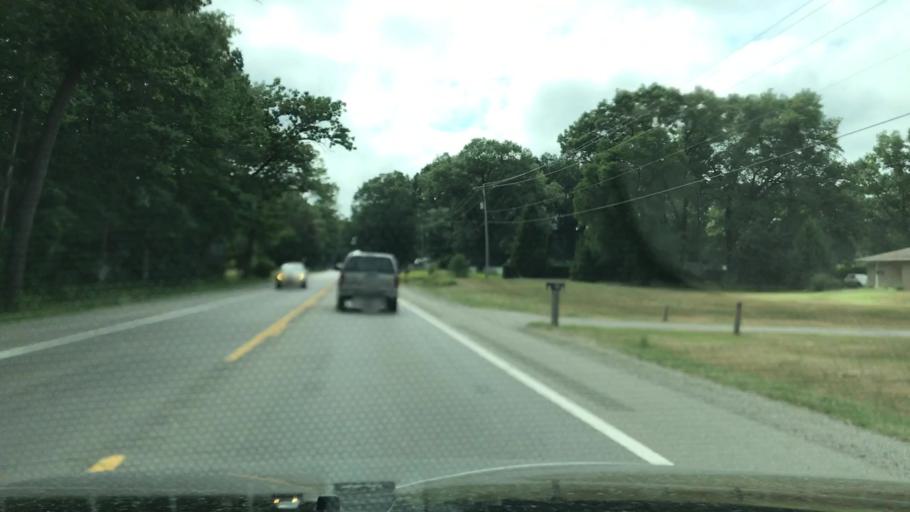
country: US
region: Michigan
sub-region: Muskegon County
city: Fruitport
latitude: 43.0739
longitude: -86.1355
